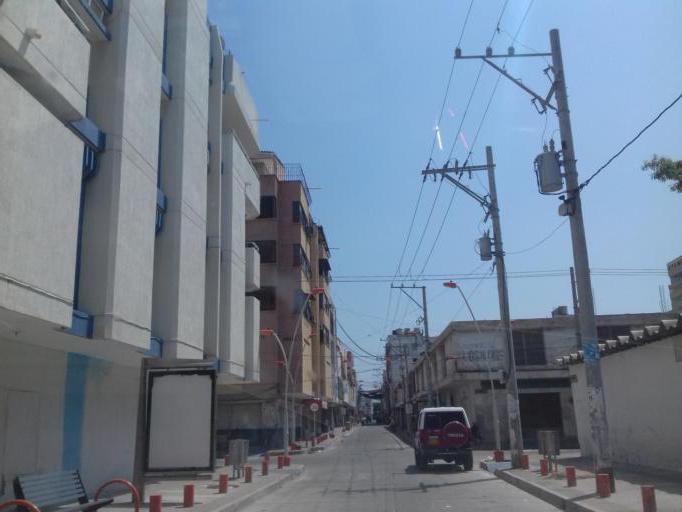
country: CO
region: La Guajira
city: Maicao
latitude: 11.3795
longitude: -72.2374
